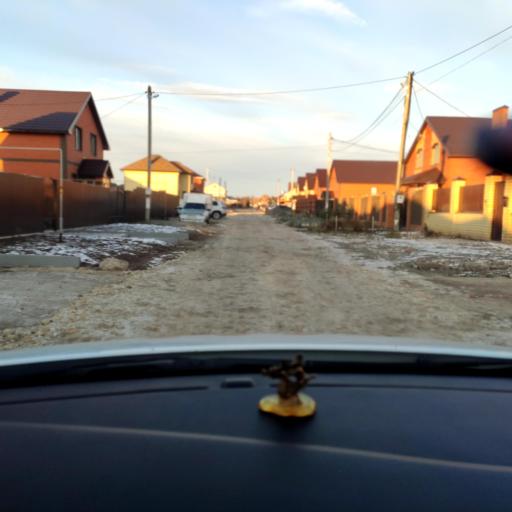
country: RU
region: Tatarstan
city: Stolbishchi
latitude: 55.6040
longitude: 49.1405
